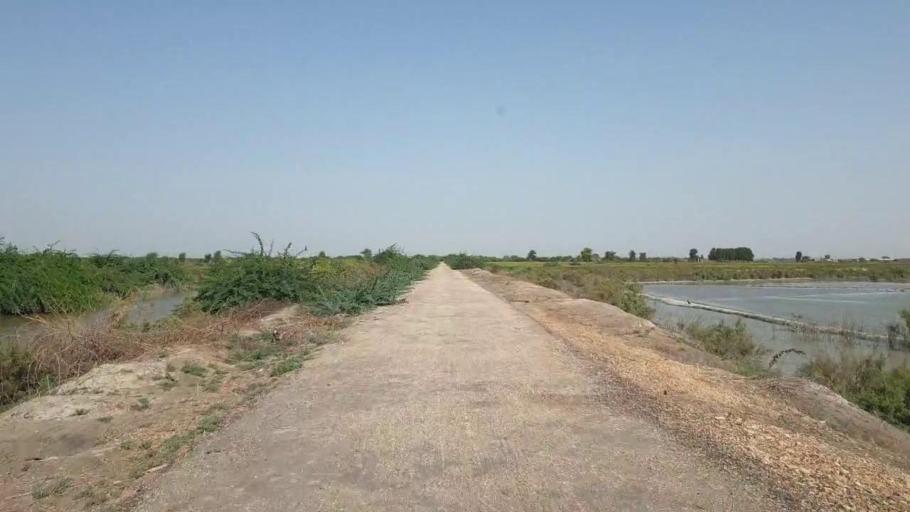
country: PK
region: Sindh
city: Tando Bago
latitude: 24.7159
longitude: 69.0726
